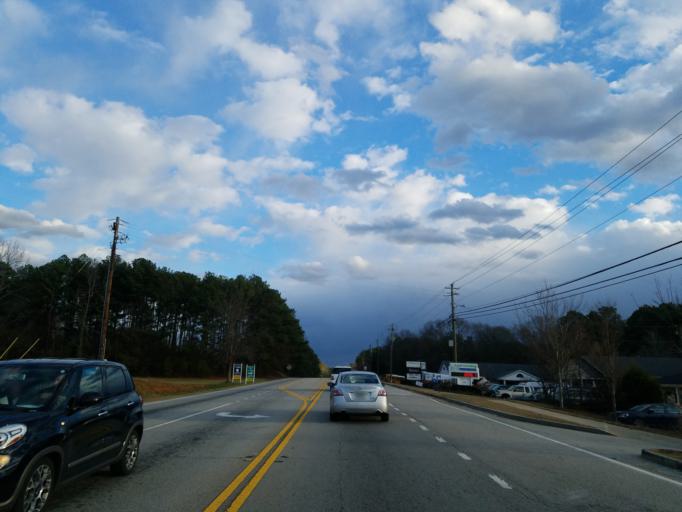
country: US
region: Georgia
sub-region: Henry County
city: McDonough
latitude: 33.4889
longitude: -84.1744
